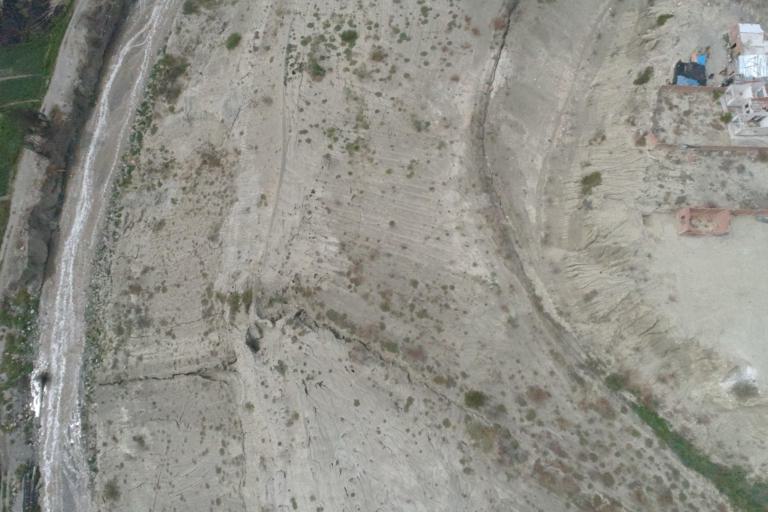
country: BO
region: La Paz
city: La Paz
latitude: -16.5985
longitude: -68.0670
